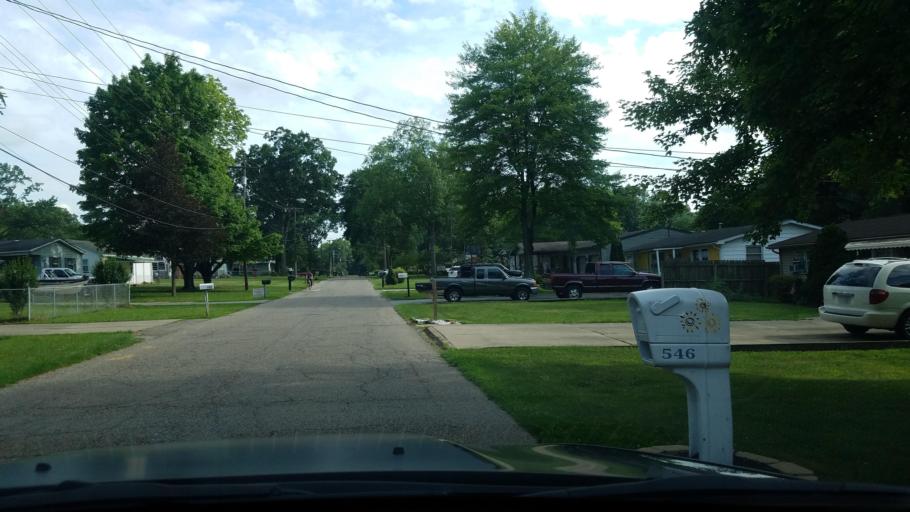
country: US
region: Ohio
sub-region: Trumbull County
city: Niles
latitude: 41.1740
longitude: -80.7803
